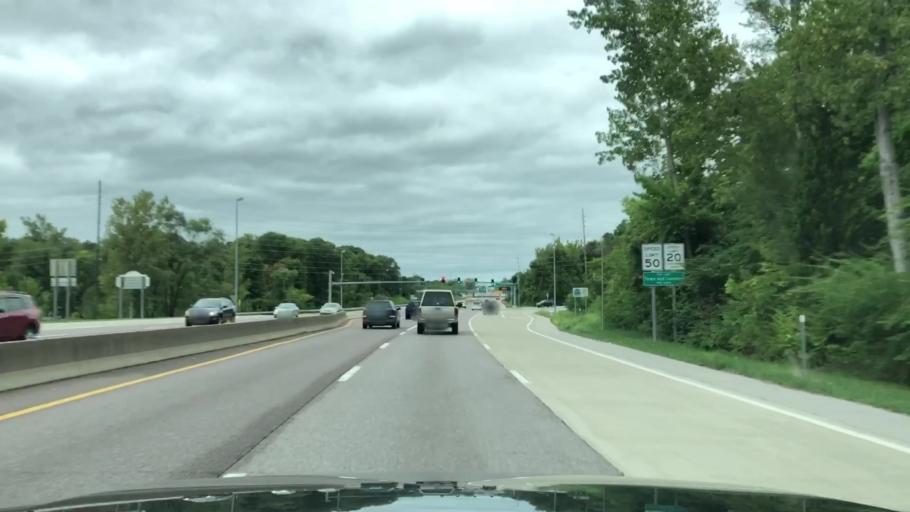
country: US
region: Missouri
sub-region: Saint Louis County
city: Manchester
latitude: 38.6508
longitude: -90.5073
